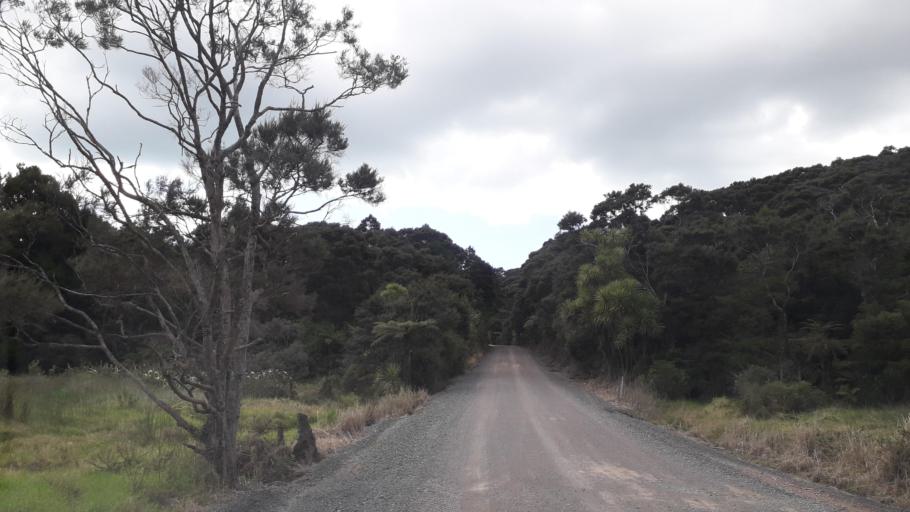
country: NZ
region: Northland
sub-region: Far North District
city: Paihia
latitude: -35.3139
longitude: 174.2242
